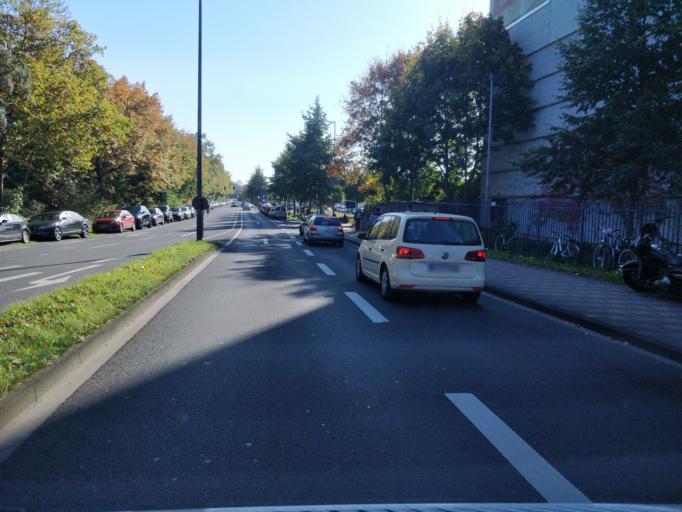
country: DE
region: North Rhine-Westphalia
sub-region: Regierungsbezirk Koln
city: Bilderstoeckchen
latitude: 50.9864
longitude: 6.9009
